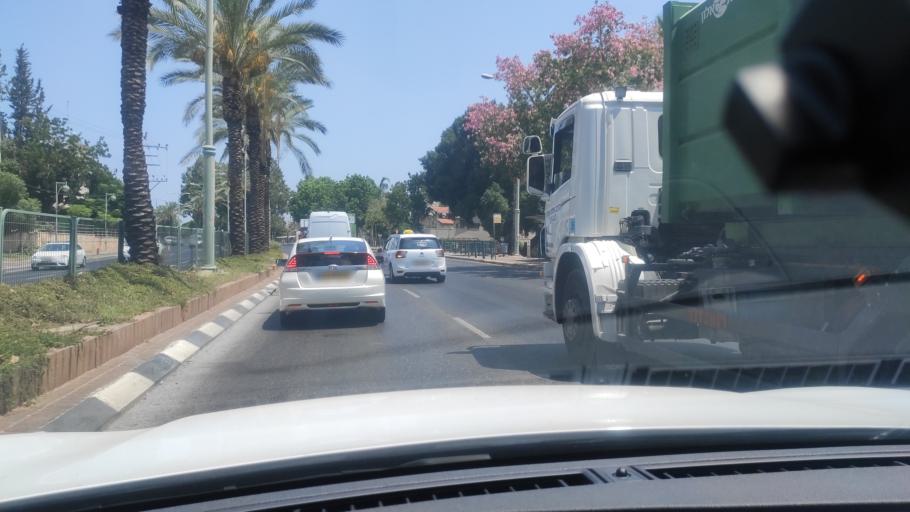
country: IL
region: Central District
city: Petah Tiqwa
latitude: 32.0911
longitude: 34.9022
